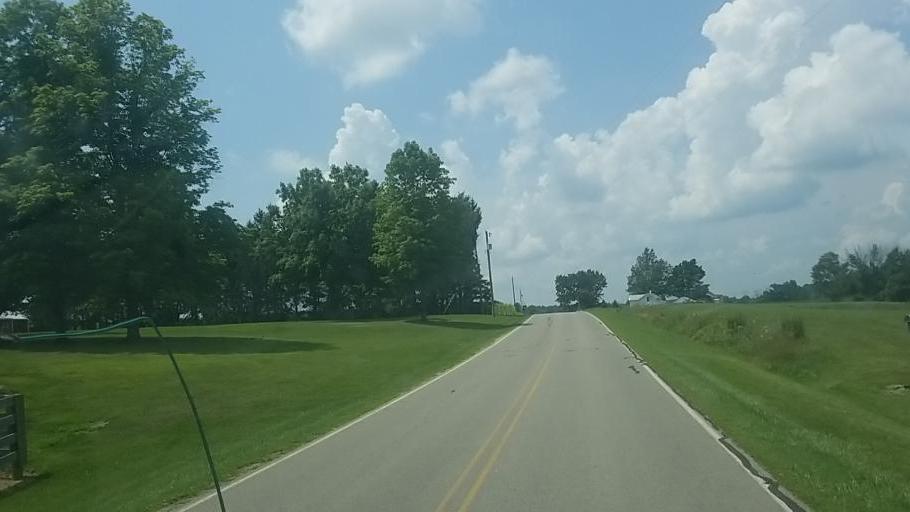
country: US
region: Ohio
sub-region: Crawford County
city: Bucyrus
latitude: 40.7672
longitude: -83.0431
